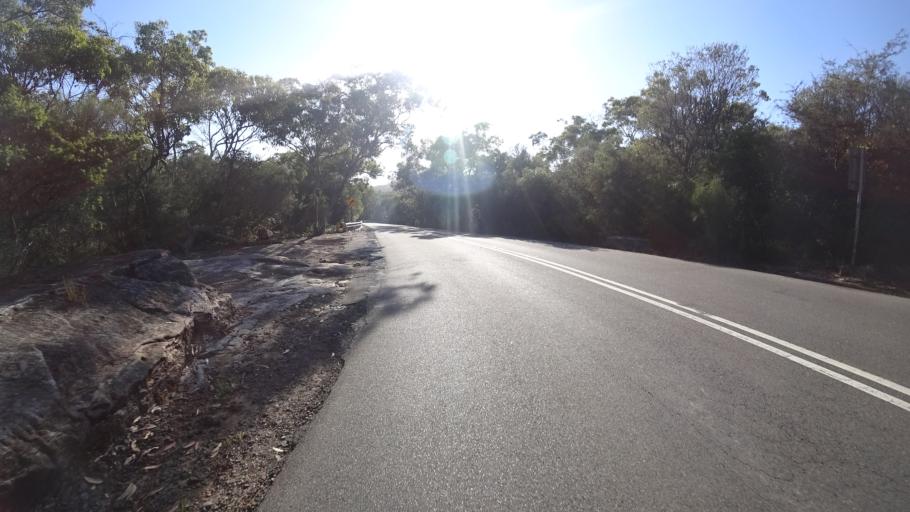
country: AU
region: New South Wales
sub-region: Pittwater
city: Ingleside
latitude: -33.6630
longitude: 151.2507
